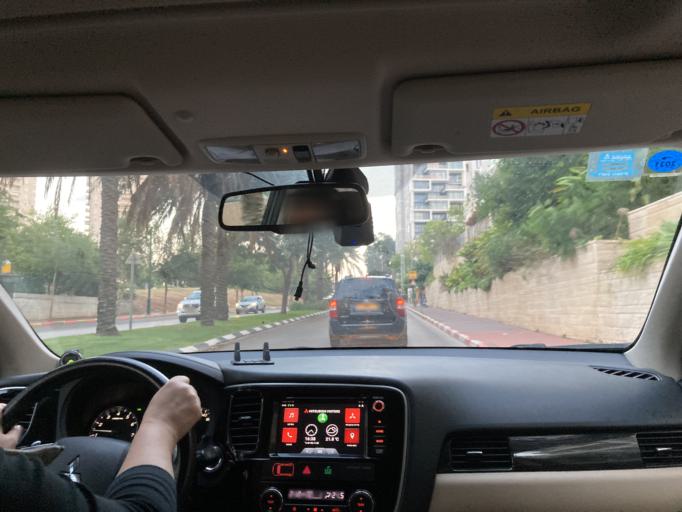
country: IL
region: Tel Aviv
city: Ramat HaSharon
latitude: 32.1561
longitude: 34.8382
